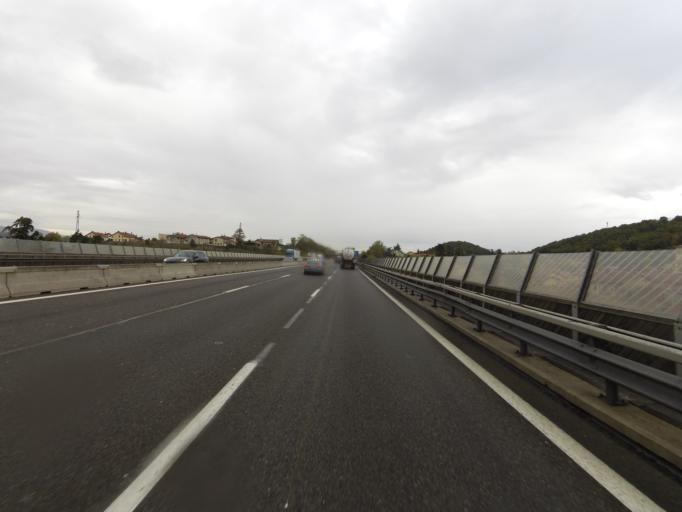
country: FR
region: Rhone-Alpes
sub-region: Departement de l'Isere
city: Chasse-sur-Rhone
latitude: 45.5788
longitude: 4.8029
